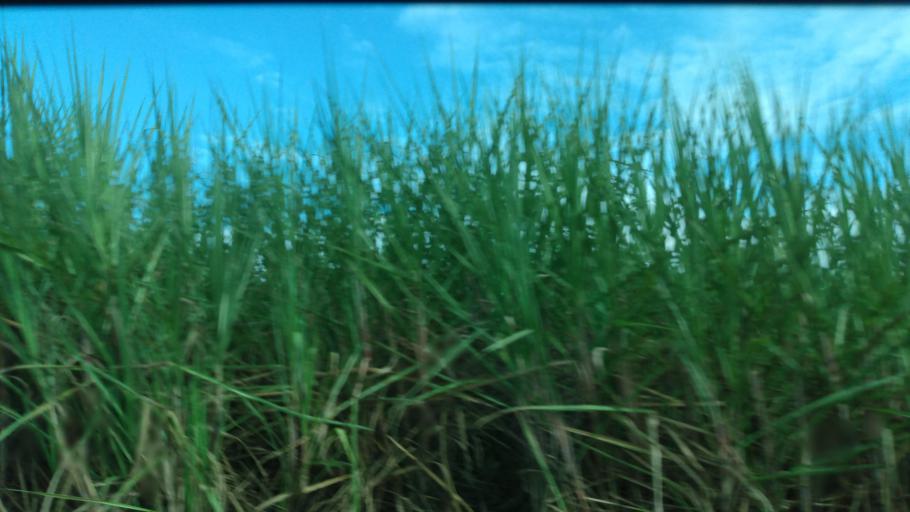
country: BR
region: Pernambuco
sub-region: Palmares
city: Palmares
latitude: -8.6916
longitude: -35.6347
